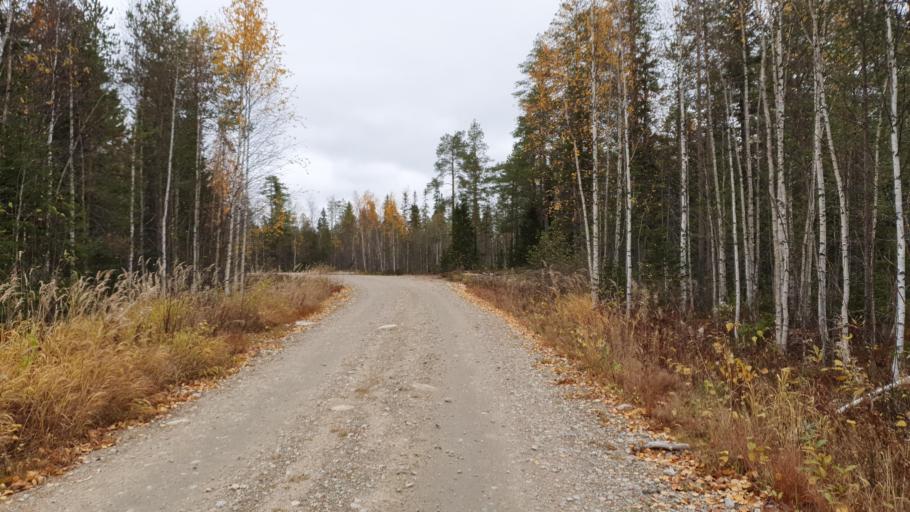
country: FI
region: Kainuu
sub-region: Kehys-Kainuu
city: Kuhmo
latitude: 64.4597
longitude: 29.6068
